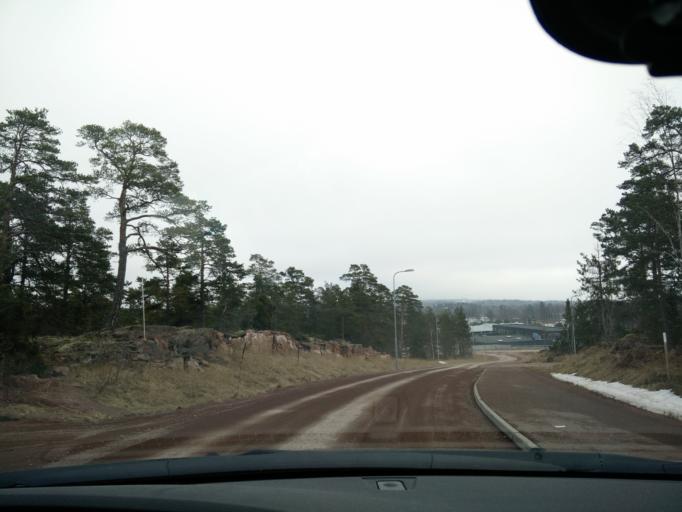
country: AX
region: Alands landsbygd
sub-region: Jomala
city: Jomala
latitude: 60.1322
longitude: 19.9304
